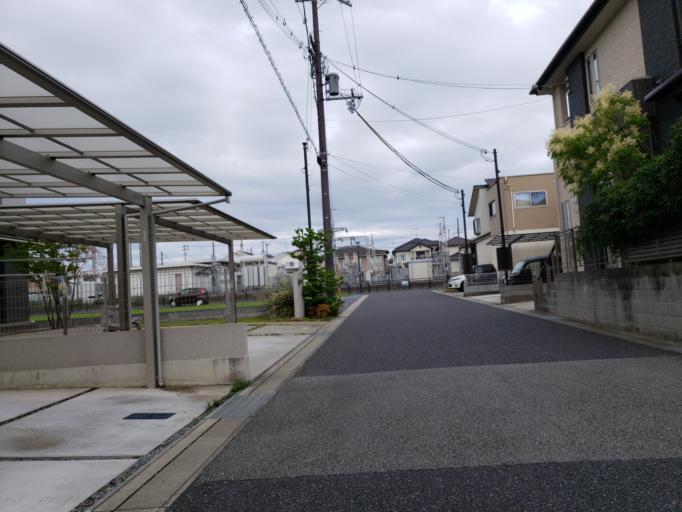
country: JP
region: Hyogo
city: Kakogawacho-honmachi
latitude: 34.7575
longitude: 134.8535
